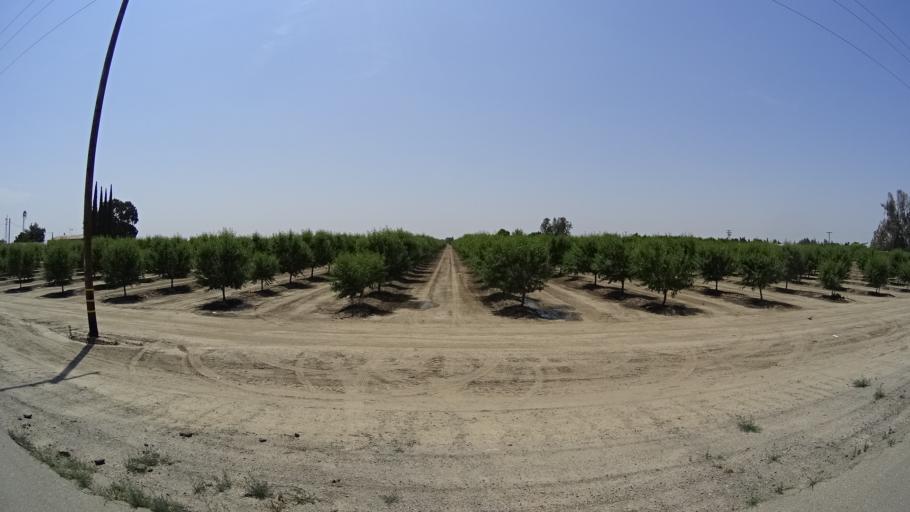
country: US
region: California
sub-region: Kings County
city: Armona
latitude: 36.3281
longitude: -119.7032
